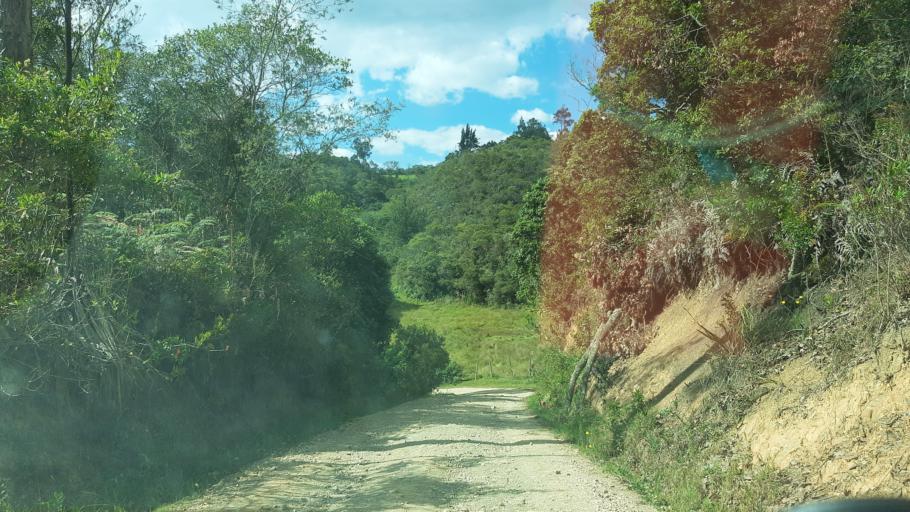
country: CO
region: Boyaca
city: La Capilla
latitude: 5.7175
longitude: -73.5356
